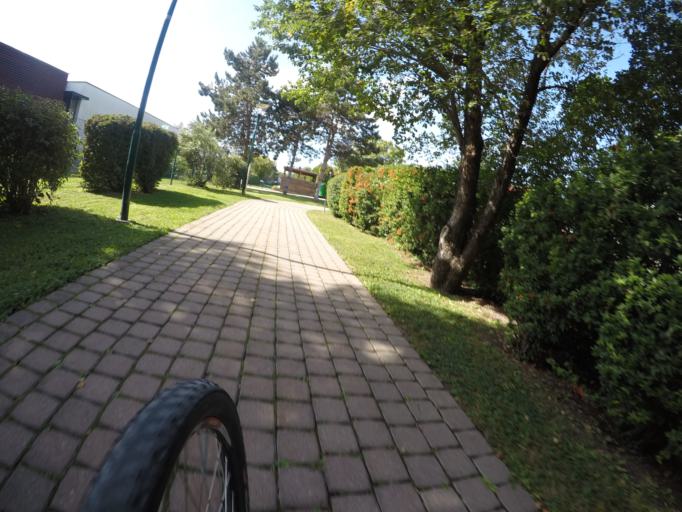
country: AT
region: Lower Austria
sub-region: Politischer Bezirk Modling
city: Wiener Neudorf
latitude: 48.0880
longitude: 16.3204
